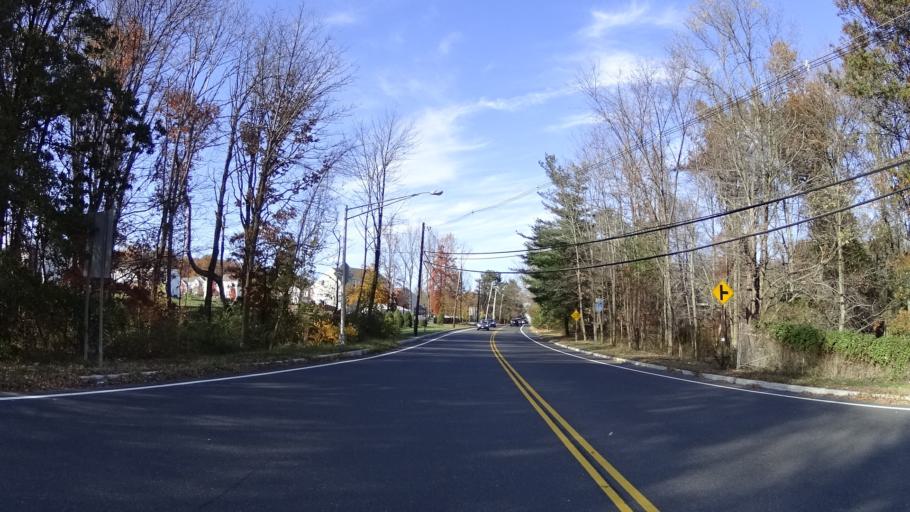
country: US
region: New Jersey
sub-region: Somerset County
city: Watchung
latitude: 40.6532
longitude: -74.4553
